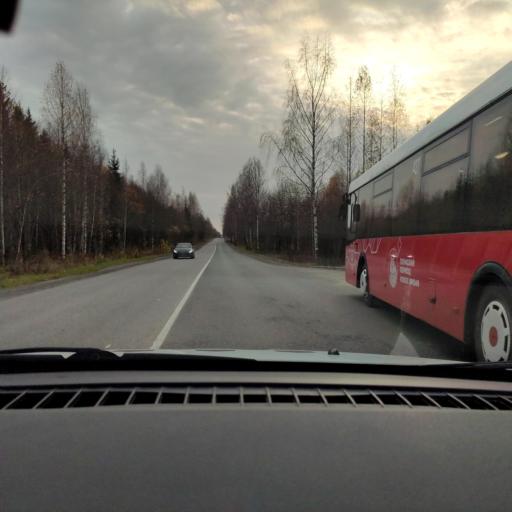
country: RU
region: Perm
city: Polazna
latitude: 58.1066
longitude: 56.4188
